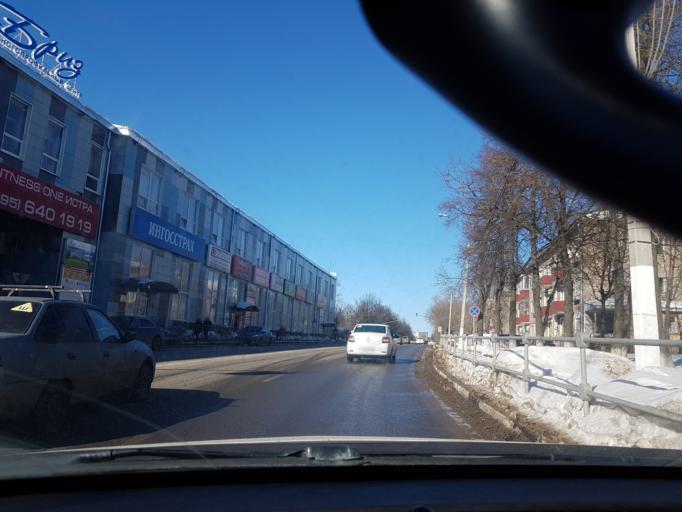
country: RU
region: Moskovskaya
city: Istra
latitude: 55.9150
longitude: 36.8580
